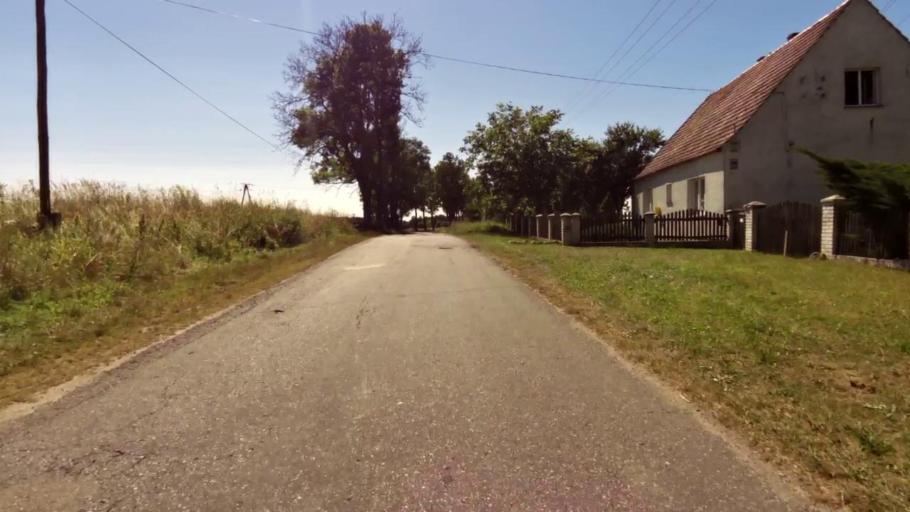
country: PL
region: West Pomeranian Voivodeship
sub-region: Powiat szczecinecki
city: Szczecinek
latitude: 53.6764
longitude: 16.5916
